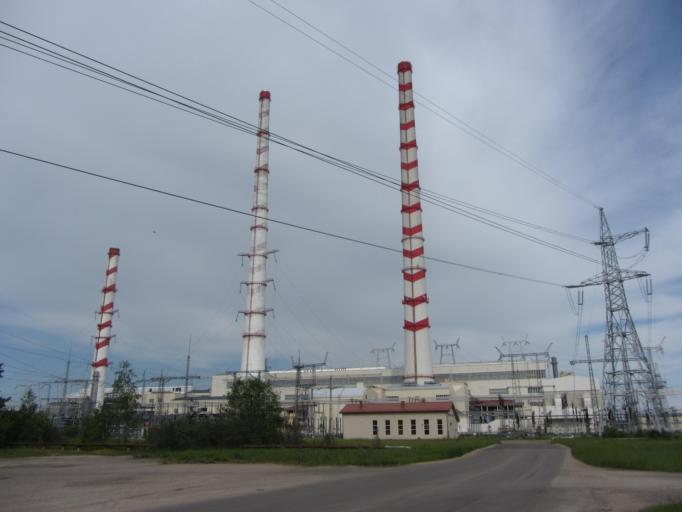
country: LT
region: Vilnius County
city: Elektrenai
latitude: 54.7686
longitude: 24.6417
